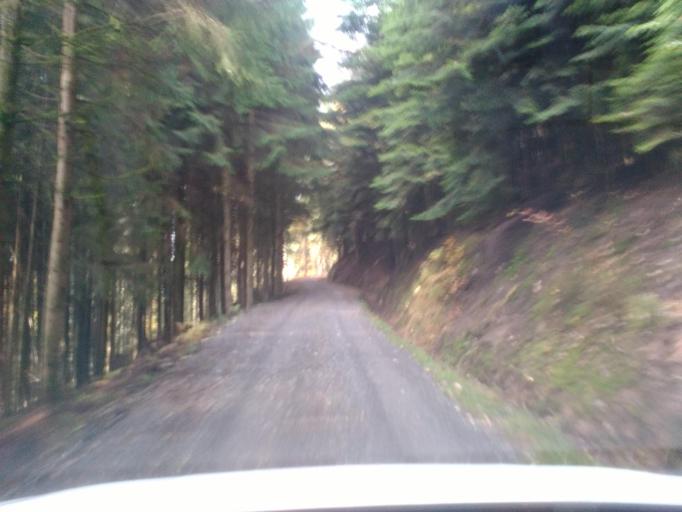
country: FR
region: Lorraine
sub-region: Departement des Vosges
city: Senones
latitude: 48.4143
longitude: 6.9805
